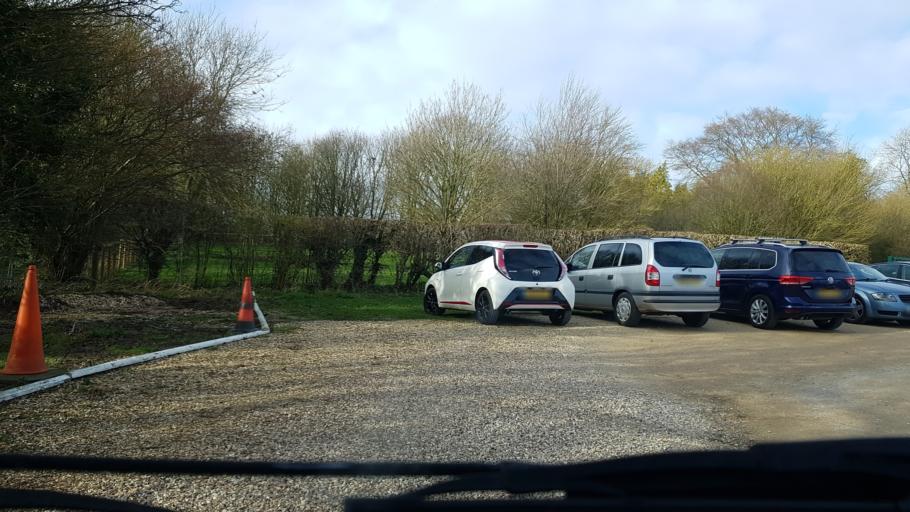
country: GB
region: England
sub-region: Wiltshire
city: Avebury
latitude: 51.4259
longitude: -1.8585
